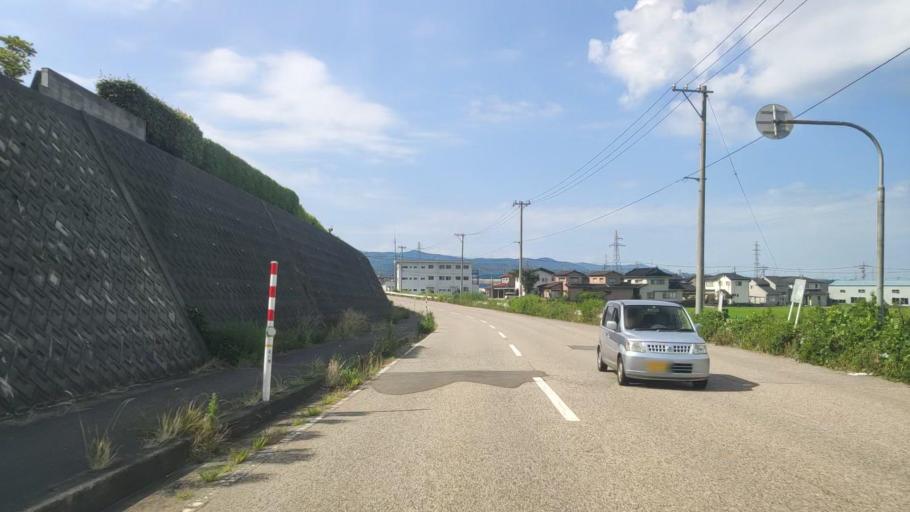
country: JP
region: Ishikawa
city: Tsurugi-asahimachi
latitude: 36.4781
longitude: 136.6160
